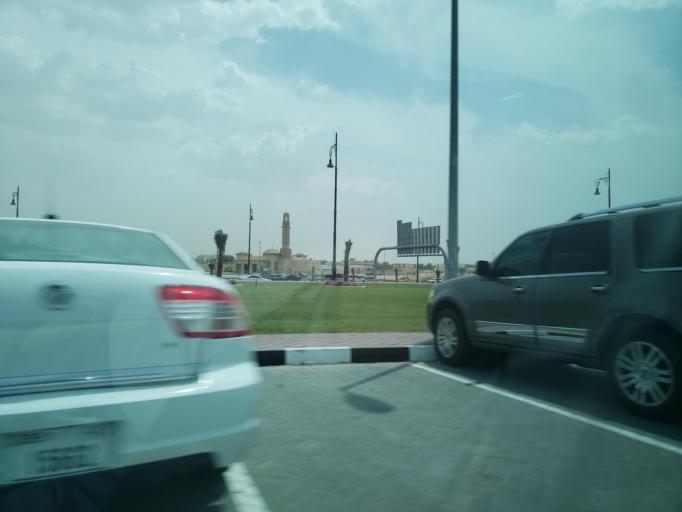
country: AE
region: Ash Shariqah
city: Sharjah
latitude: 25.3064
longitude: 55.5868
